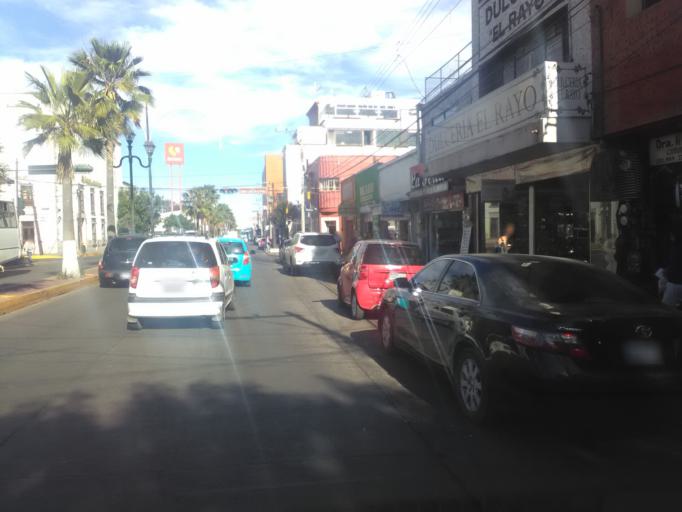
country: MX
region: Durango
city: Victoria de Durango
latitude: 24.0256
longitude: -104.6647
